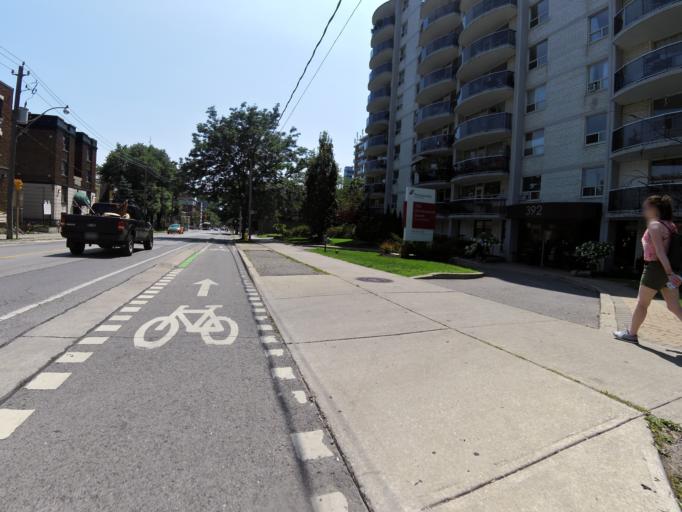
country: CA
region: Ontario
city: Toronto
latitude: 43.6643
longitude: -79.3736
